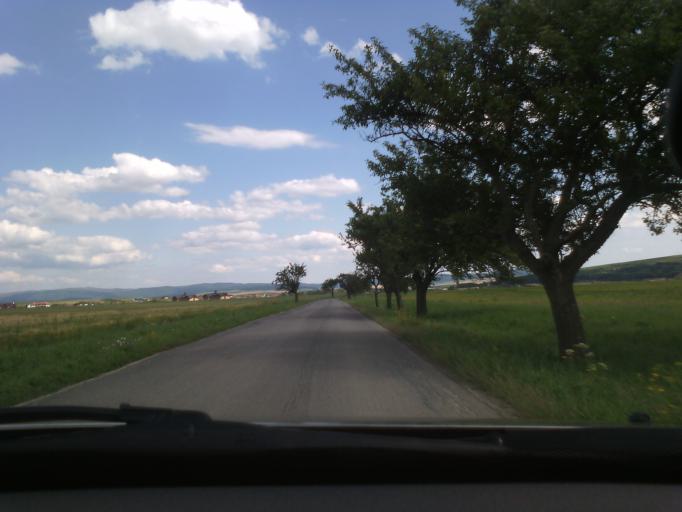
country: SK
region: Presovsky
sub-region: Okres Poprad
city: Nova Lesna
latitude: 49.1265
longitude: 20.3319
